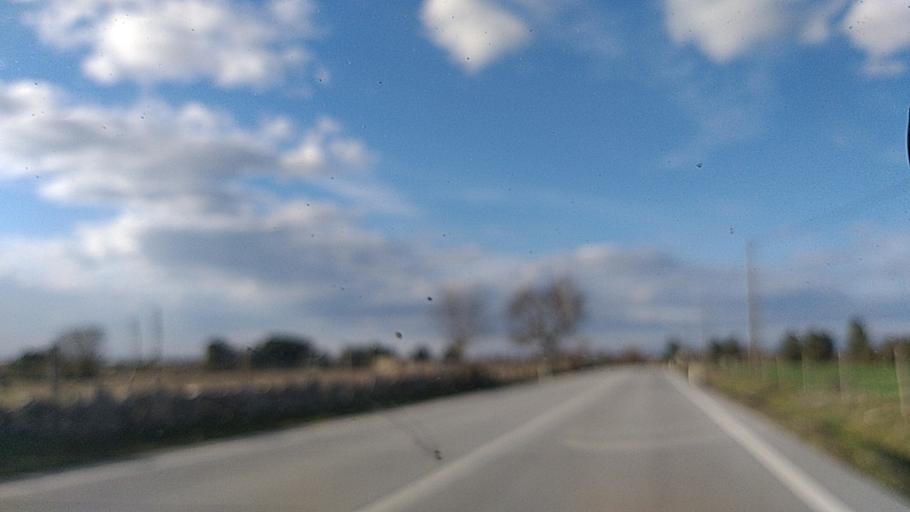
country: ES
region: Castille and Leon
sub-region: Provincia de Salamanca
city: Fuentes de Onoro
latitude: 40.6344
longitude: -6.8548
